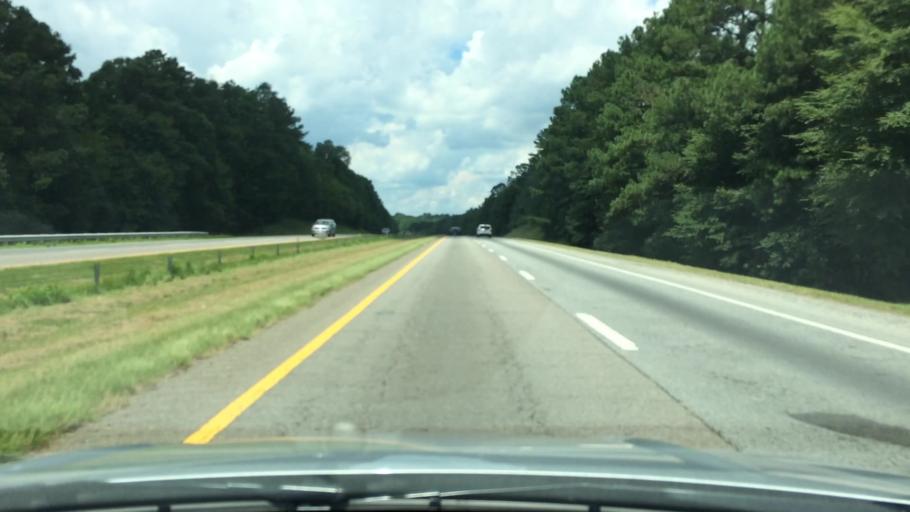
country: US
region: South Carolina
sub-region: Newberry County
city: Prosperity
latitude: 34.2713
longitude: -81.5116
